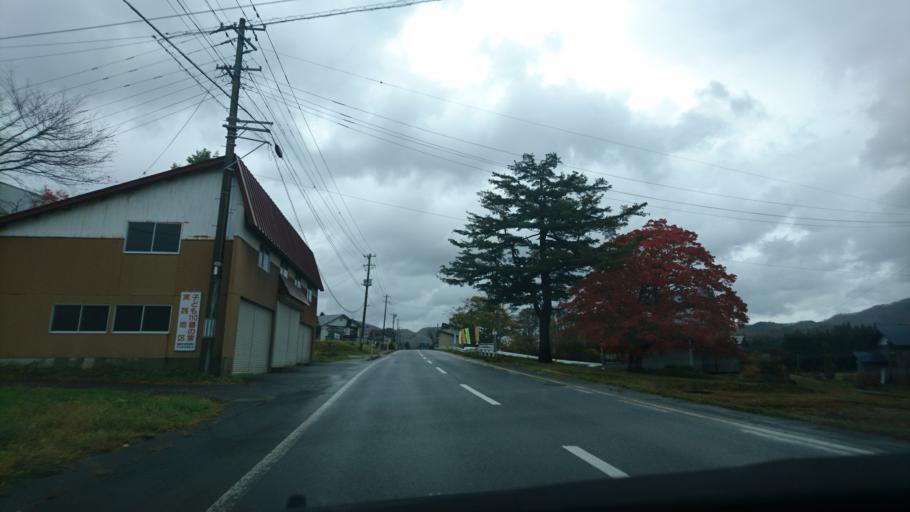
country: JP
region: Akita
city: Kakunodatemachi
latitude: 39.4611
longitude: 140.7753
